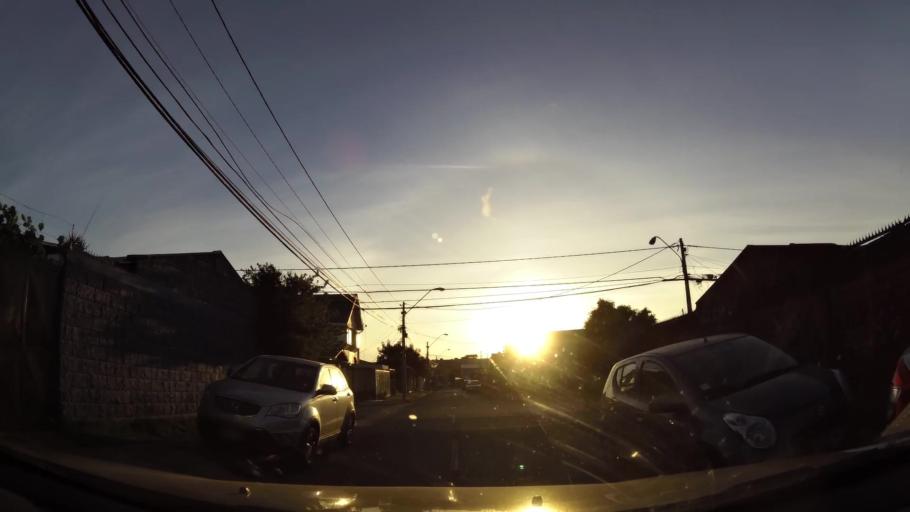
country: CL
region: Santiago Metropolitan
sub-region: Provincia de Cordillera
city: Puente Alto
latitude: -33.5997
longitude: -70.5708
